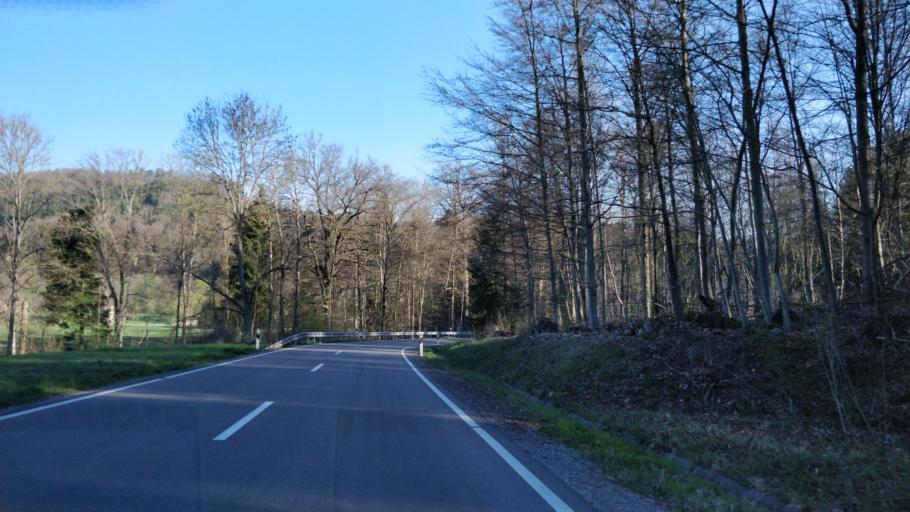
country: DE
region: Baden-Wuerttemberg
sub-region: Regierungsbezirk Stuttgart
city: Oberrot
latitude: 49.0443
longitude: 9.7071
